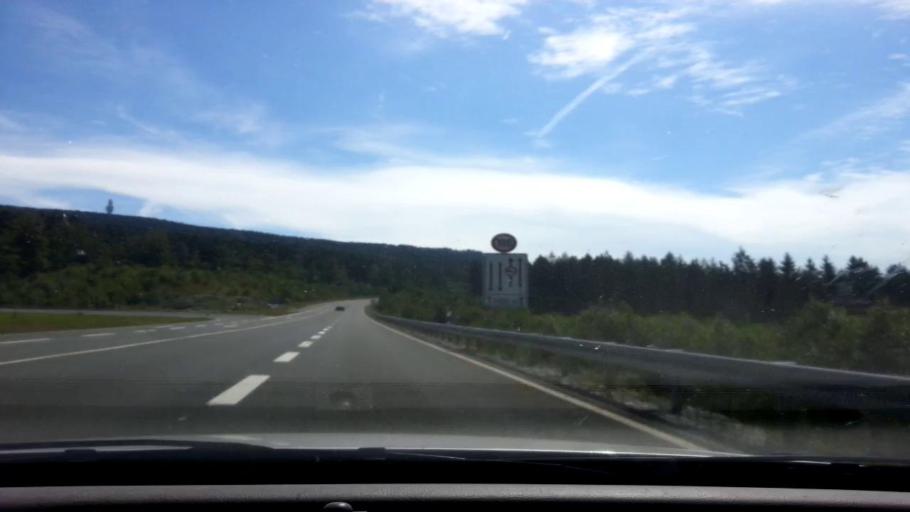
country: DE
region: Bavaria
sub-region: Upper Franconia
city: Fichtelberg
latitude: 50.0464
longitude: 11.8340
